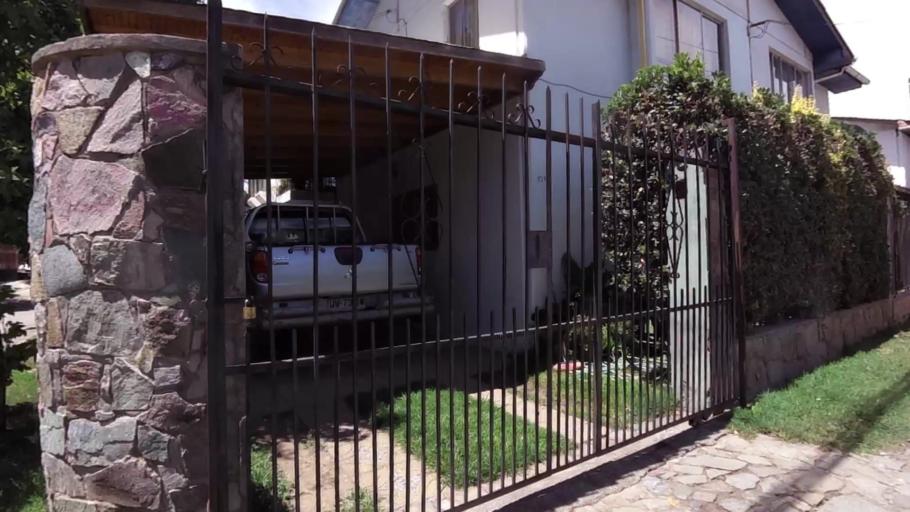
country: CL
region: O'Higgins
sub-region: Provincia de Cachapoal
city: Graneros
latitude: -34.0605
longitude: -70.7289
